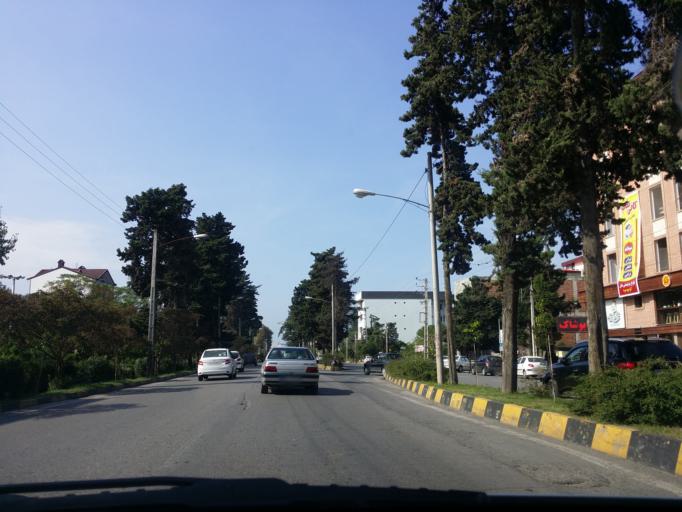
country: IR
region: Mazandaran
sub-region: Nowshahr
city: Nowshahr
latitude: 36.6552
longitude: 51.4912
